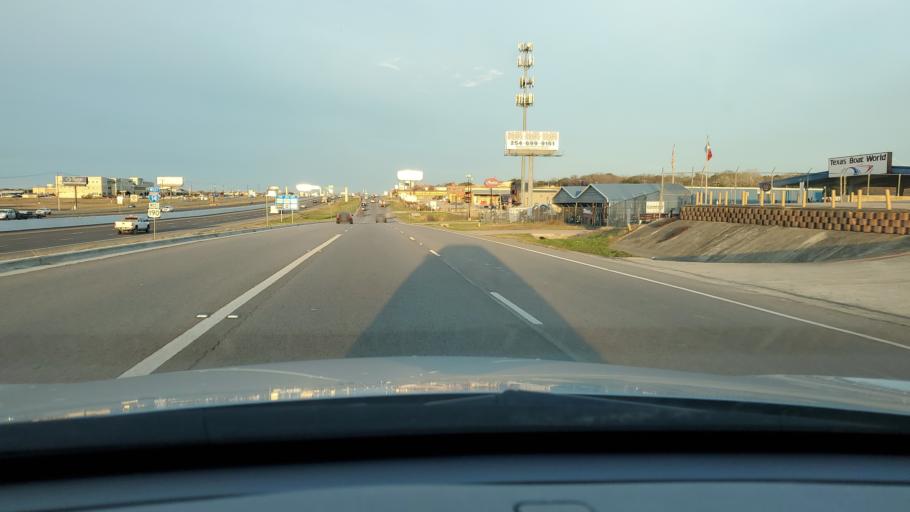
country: US
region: Texas
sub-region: Bell County
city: Harker Heights
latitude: 31.0726
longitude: -97.6753
